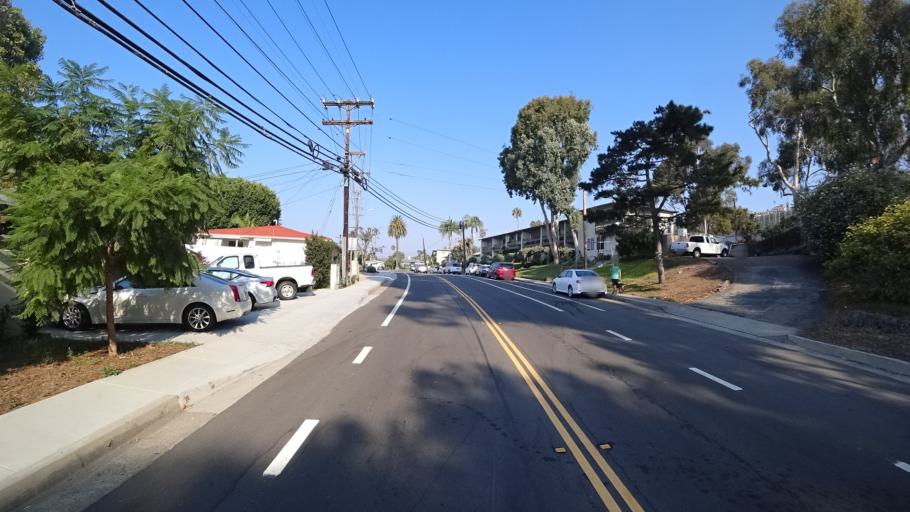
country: US
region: California
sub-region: Orange County
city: San Clemente
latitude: 33.4178
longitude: -117.6055
